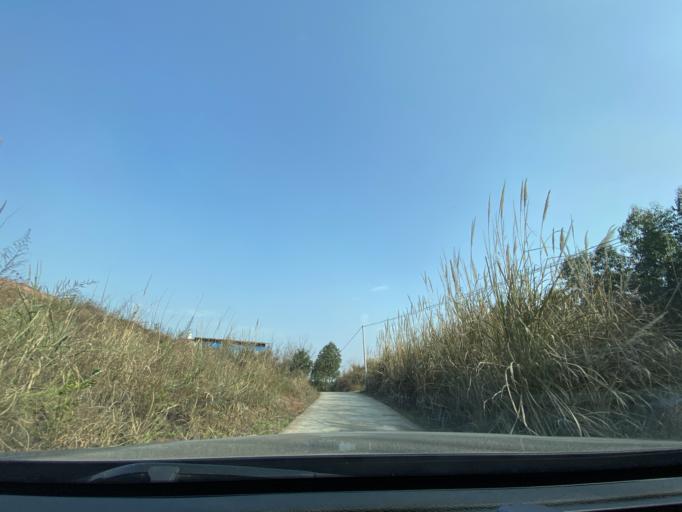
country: CN
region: Sichuan
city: Wenlin
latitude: 30.2482
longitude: 104.2466
